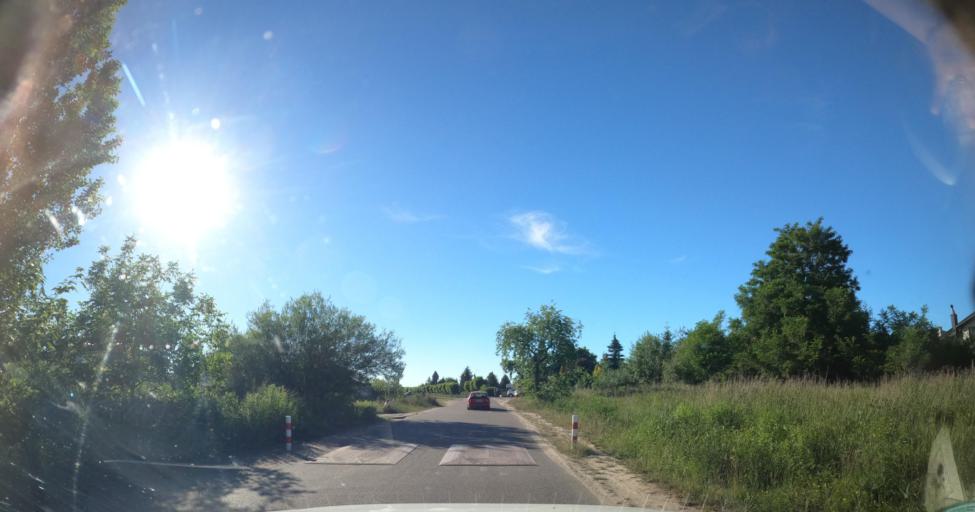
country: PL
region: West Pomeranian Voivodeship
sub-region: Szczecin
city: Szczecin
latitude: 53.4779
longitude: 14.5348
